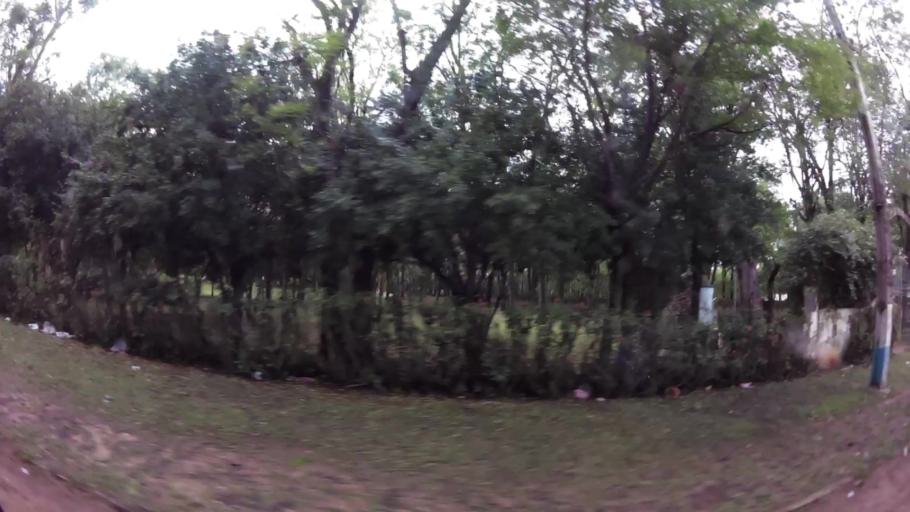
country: PY
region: Central
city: Limpio
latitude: -25.1357
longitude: -57.4722
